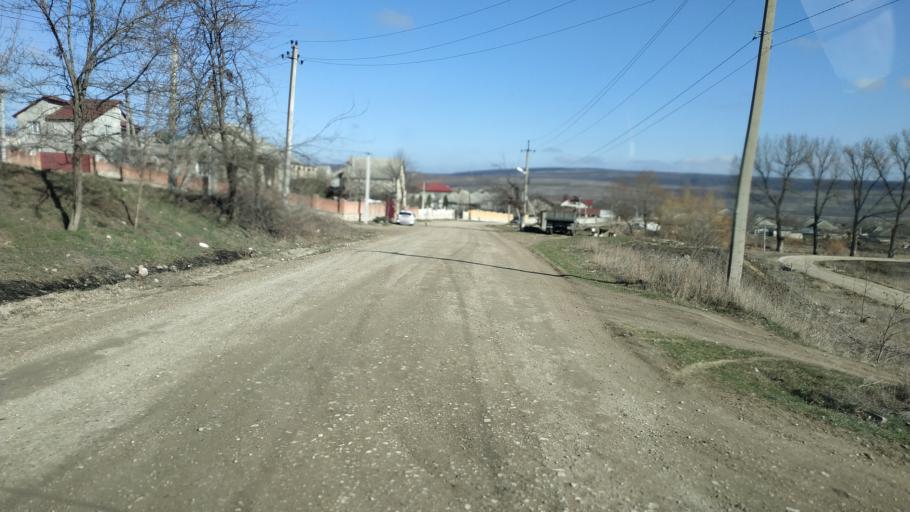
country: MD
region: Hincesti
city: Hincesti
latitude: 46.9305
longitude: 28.6347
